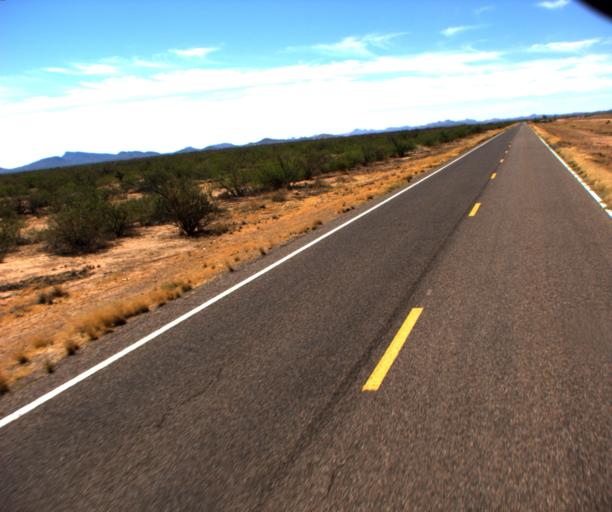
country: US
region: Arizona
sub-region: Yavapai County
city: Congress
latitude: 33.9616
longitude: -113.1416
